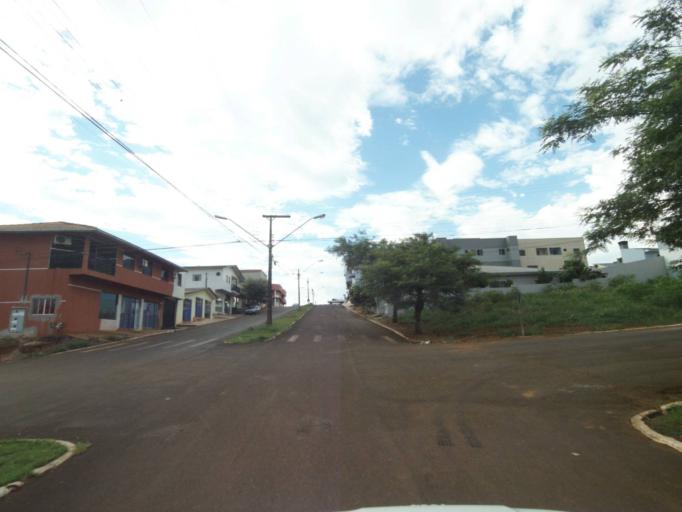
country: BR
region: Parana
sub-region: Laranjeiras Do Sul
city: Laranjeiras do Sul
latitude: -25.4930
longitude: -52.5287
